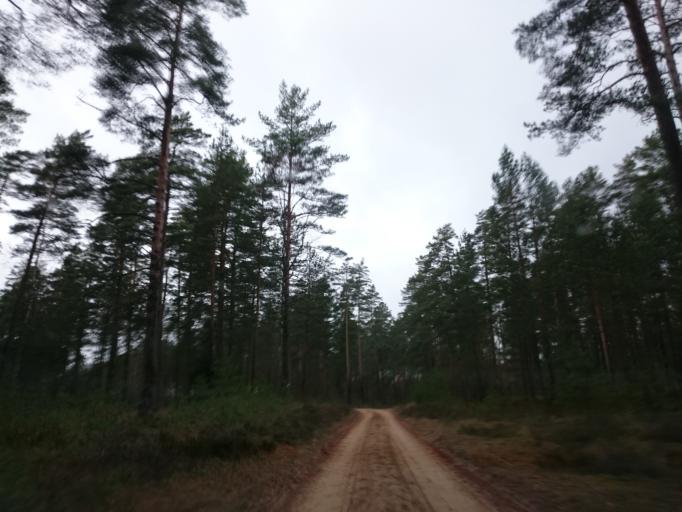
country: LV
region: Riga
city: Bergi
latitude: 57.0168
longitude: 24.3518
